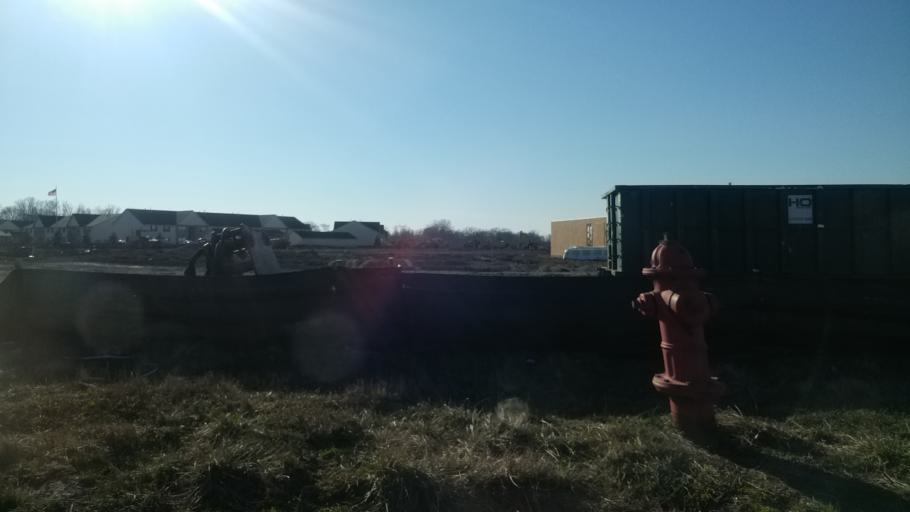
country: US
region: Ohio
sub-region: Hancock County
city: Findlay
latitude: 41.0838
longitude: -83.6688
